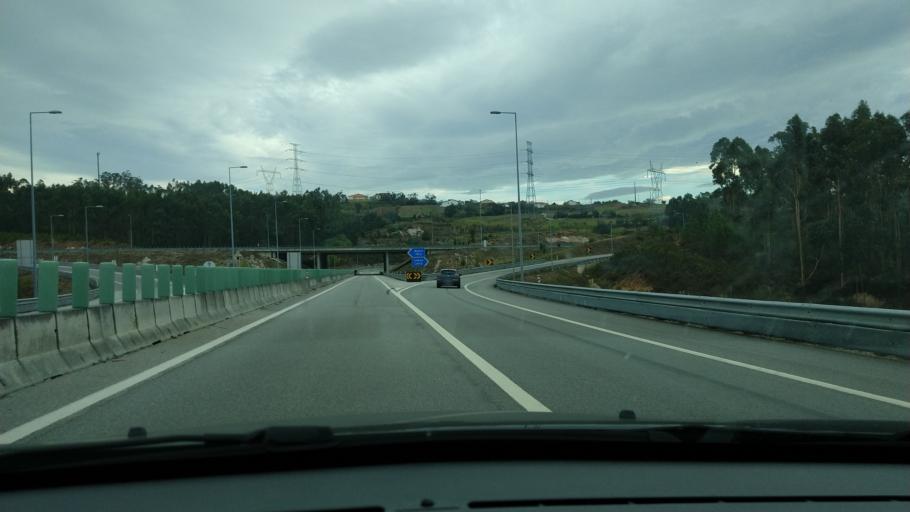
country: PT
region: Coimbra
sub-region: Figueira da Foz
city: Alhadas
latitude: 40.1574
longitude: -8.7779
